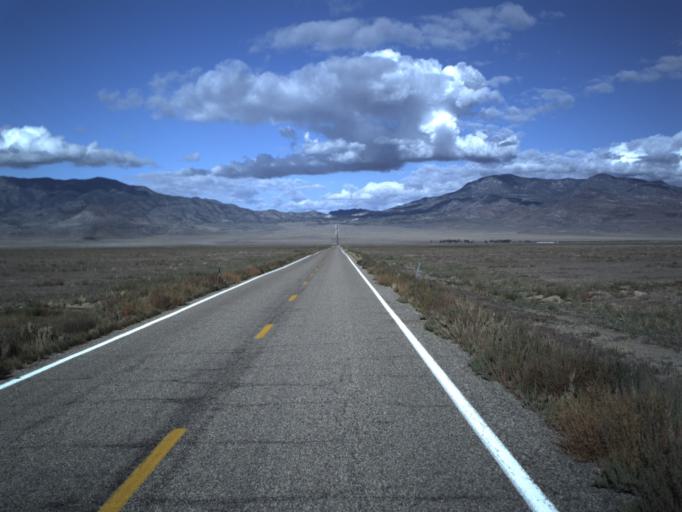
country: US
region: Utah
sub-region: Beaver County
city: Milford
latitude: 38.4610
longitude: -113.3778
